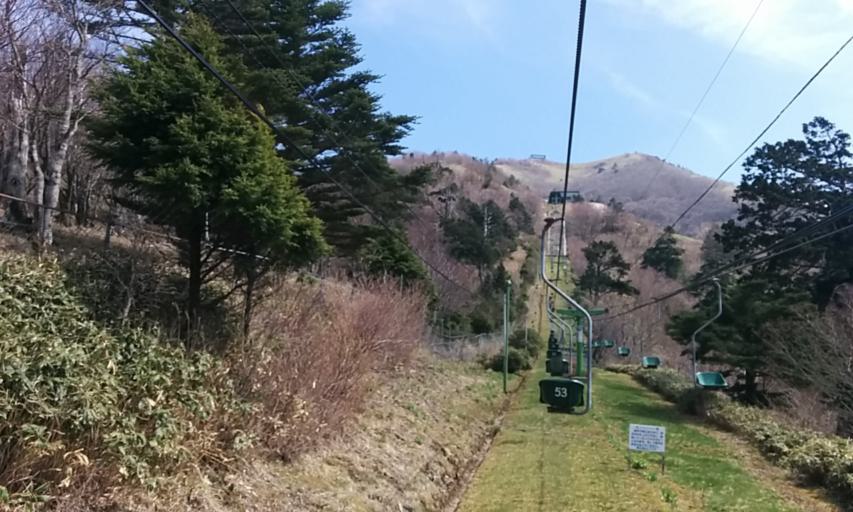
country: JP
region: Tokushima
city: Wakimachi
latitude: 33.8630
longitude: 134.0910
